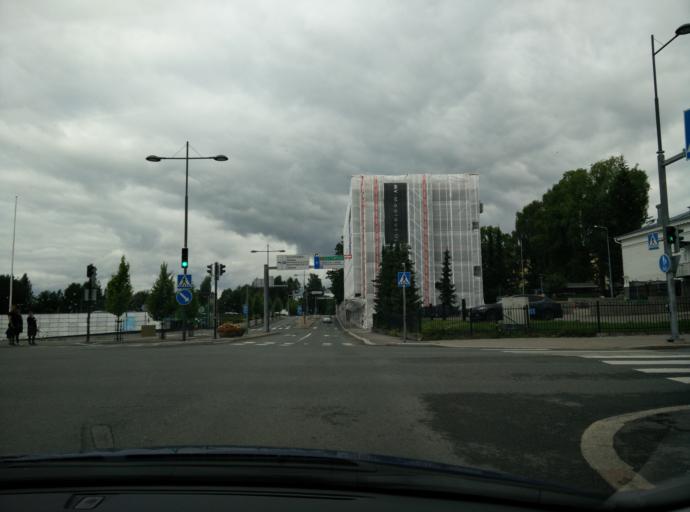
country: FI
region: Haeme
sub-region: Haemeenlinna
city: Haemeenlinna
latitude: 60.9949
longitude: 24.4574
